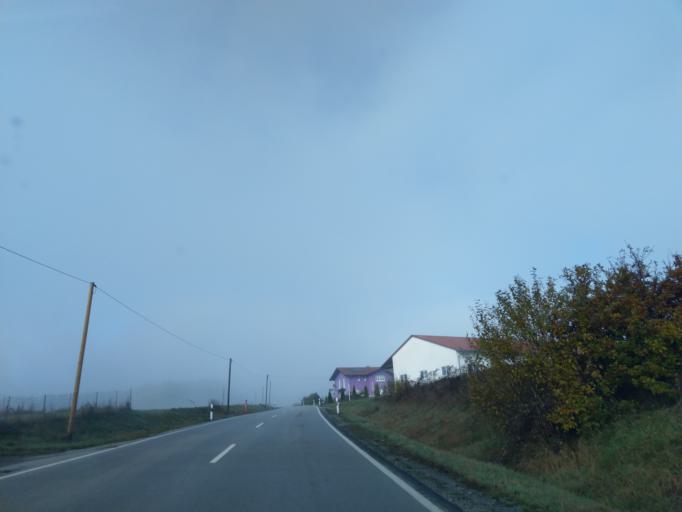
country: DE
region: Bavaria
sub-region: Lower Bavaria
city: Schollnach
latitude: 48.7328
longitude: 13.1692
